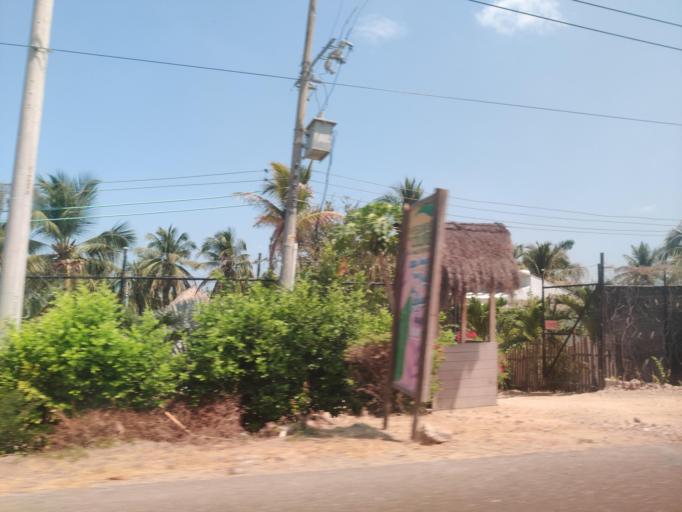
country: CO
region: Bolivar
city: Turbana
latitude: 10.2754
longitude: -75.5444
